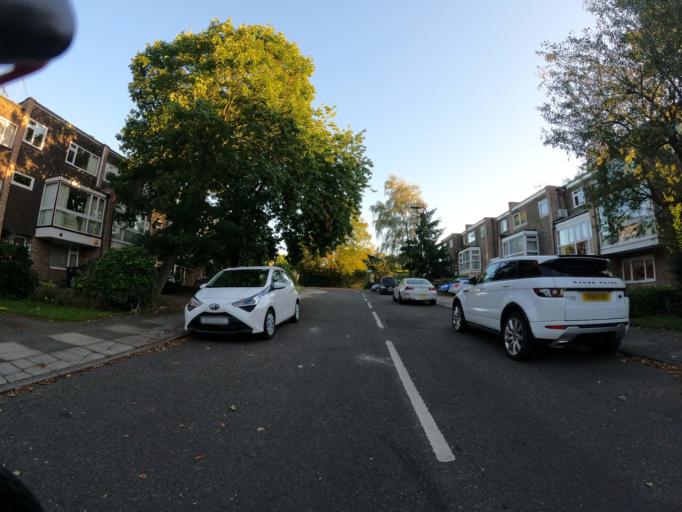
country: GB
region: England
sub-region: Greater London
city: Ealing Broadway
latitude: 51.5228
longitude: -0.3183
